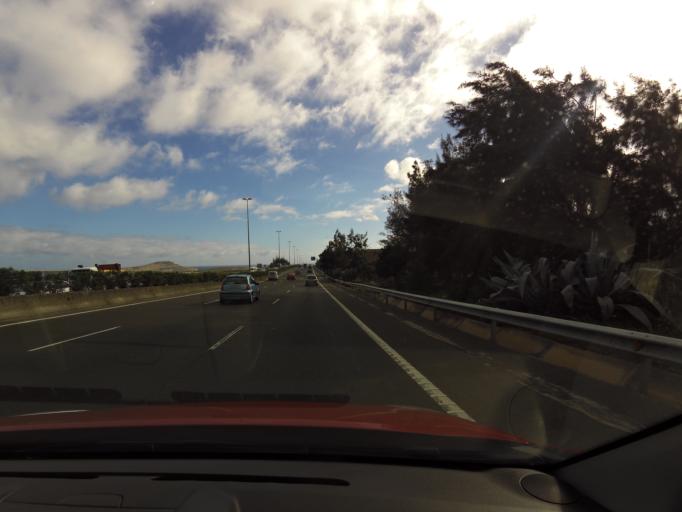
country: ES
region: Canary Islands
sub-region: Provincia de Las Palmas
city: Telde
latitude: 27.9619
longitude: -15.3894
